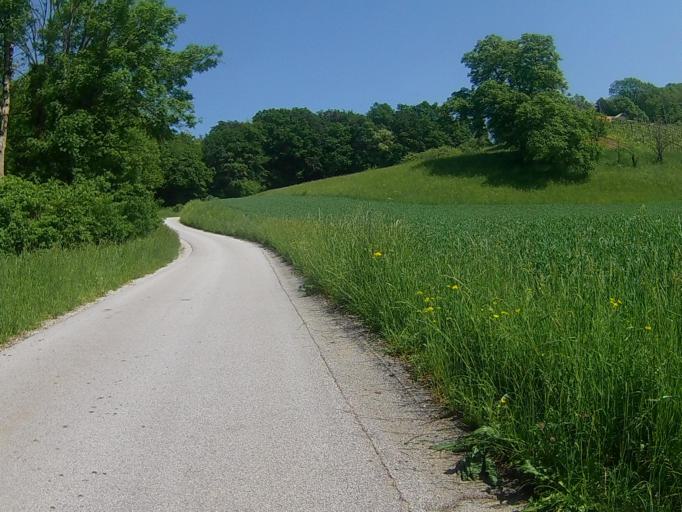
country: SI
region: Pesnica
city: Pesnica pri Mariboru
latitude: 46.5697
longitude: 15.7044
